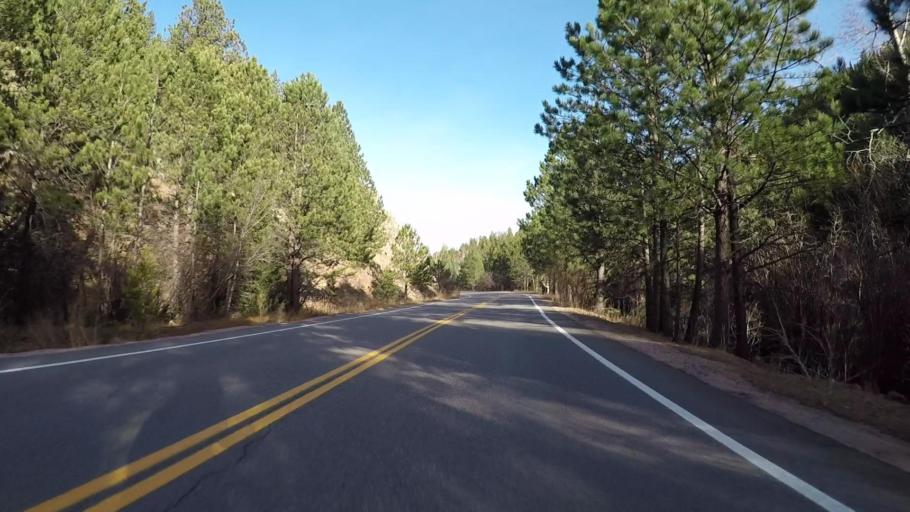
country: US
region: Colorado
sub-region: Boulder County
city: Nederland
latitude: 40.0670
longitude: -105.4494
